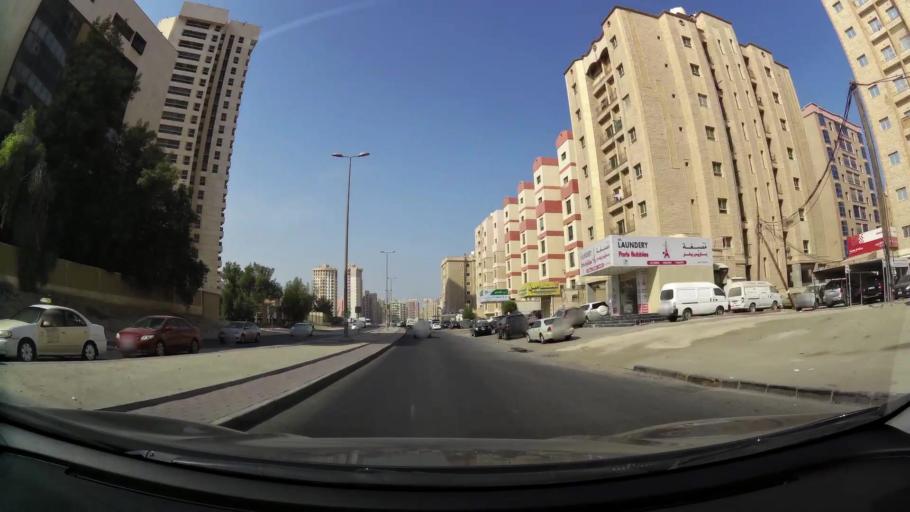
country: KW
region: Al Ahmadi
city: Al Mahbulah
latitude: 29.1391
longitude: 48.1217
